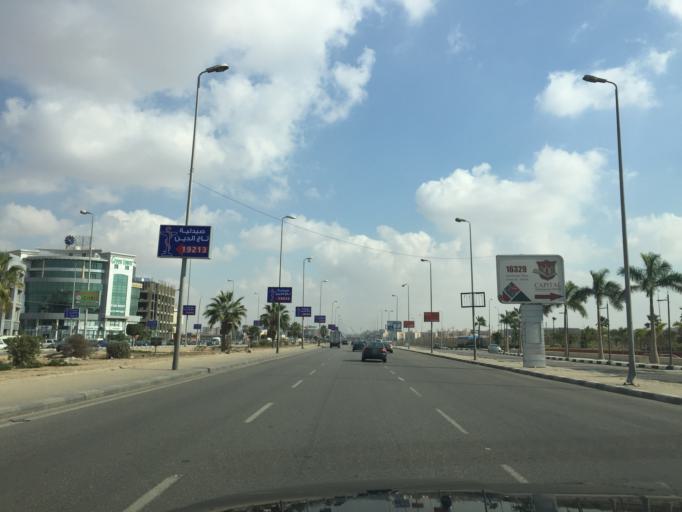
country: EG
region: Muhafazat al Qalyubiyah
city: Al Khankah
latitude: 30.0254
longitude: 31.4651
